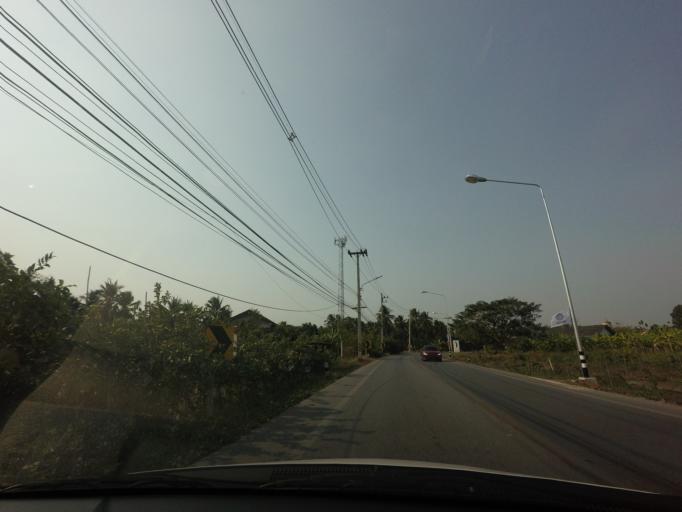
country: TH
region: Nakhon Pathom
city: Sam Phran
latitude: 13.7004
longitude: 100.2057
